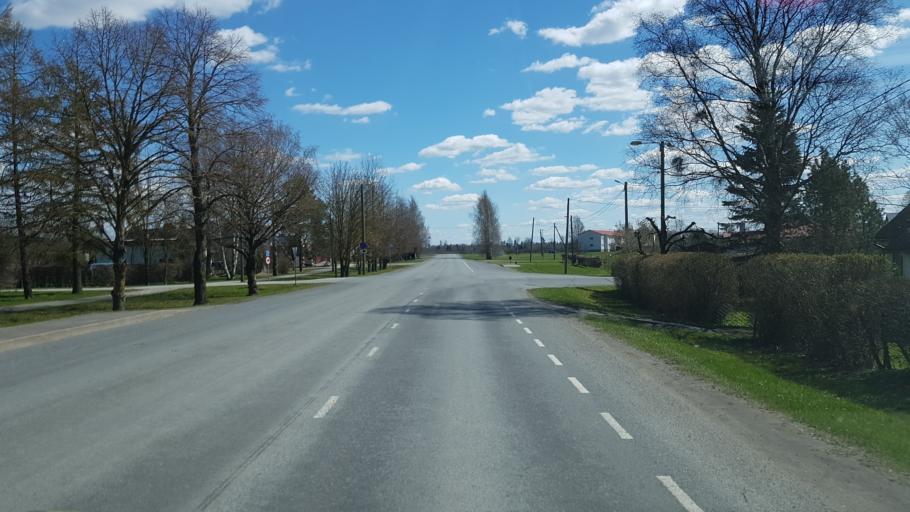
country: EE
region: Viljandimaa
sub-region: Viiratsi vald
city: Viiratsi
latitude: 58.3609
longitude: 25.6438
